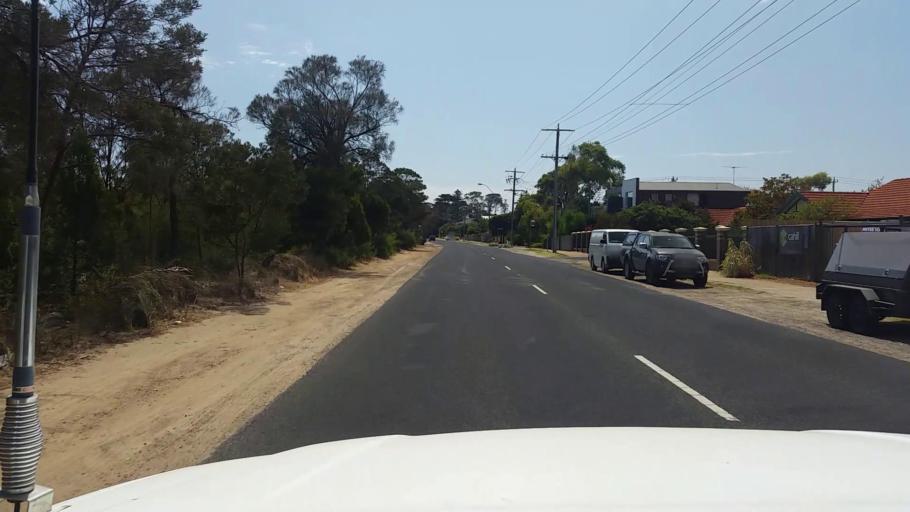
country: AU
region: Victoria
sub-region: Mornington Peninsula
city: Mount Martha
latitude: -38.2512
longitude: 145.0279
